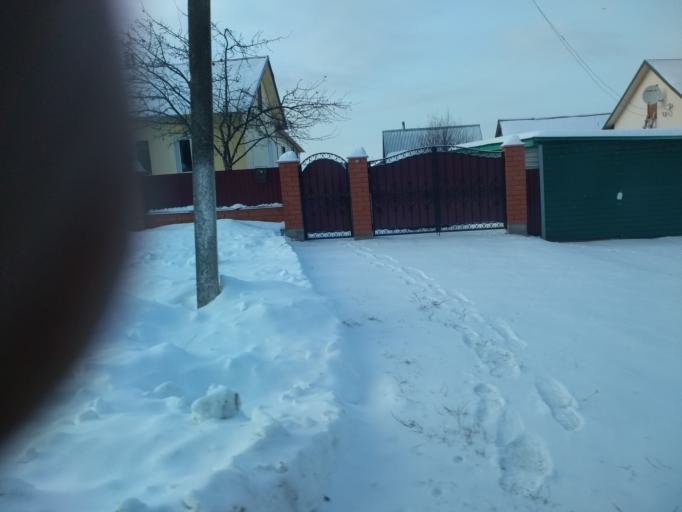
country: RU
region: Bashkortostan
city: Iglino
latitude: 54.7704
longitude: 56.5344
